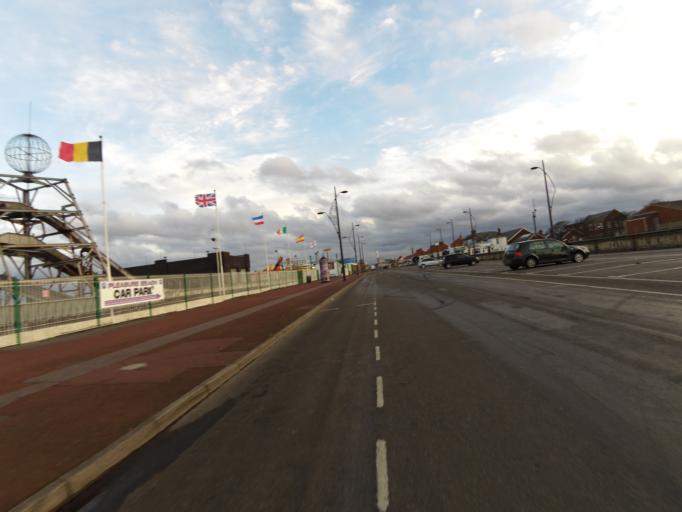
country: GB
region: England
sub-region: Norfolk
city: Great Yarmouth
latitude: 52.5962
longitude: 1.7357
